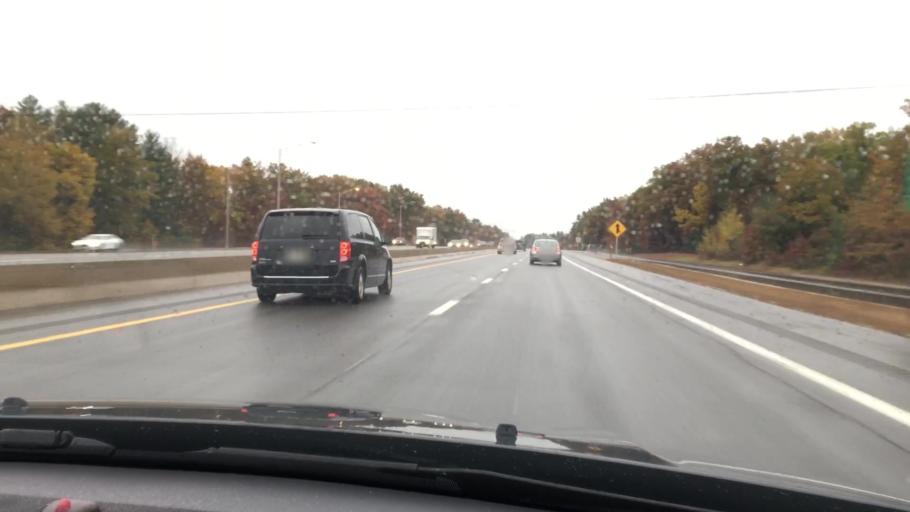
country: US
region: New Hampshire
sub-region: Hillsborough County
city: Litchfield
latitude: 42.8168
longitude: -71.4971
